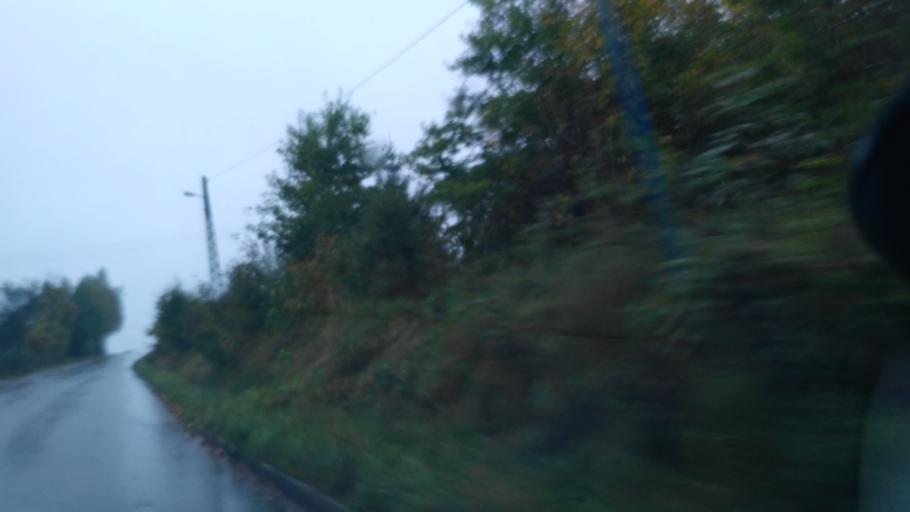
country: PL
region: Subcarpathian Voivodeship
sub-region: Powiat krosnienski
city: Kroscienko Wyzne
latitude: 49.6843
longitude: 21.8113
